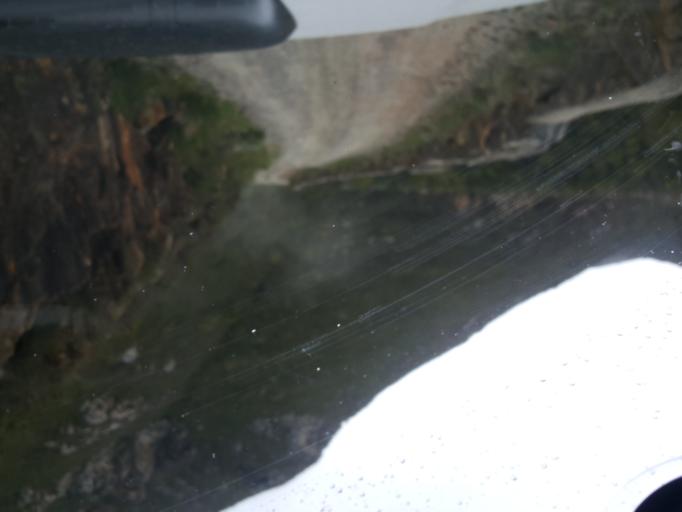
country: ZA
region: Western Cape
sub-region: Eden District Municipality
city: George
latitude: -33.8934
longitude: 22.4216
